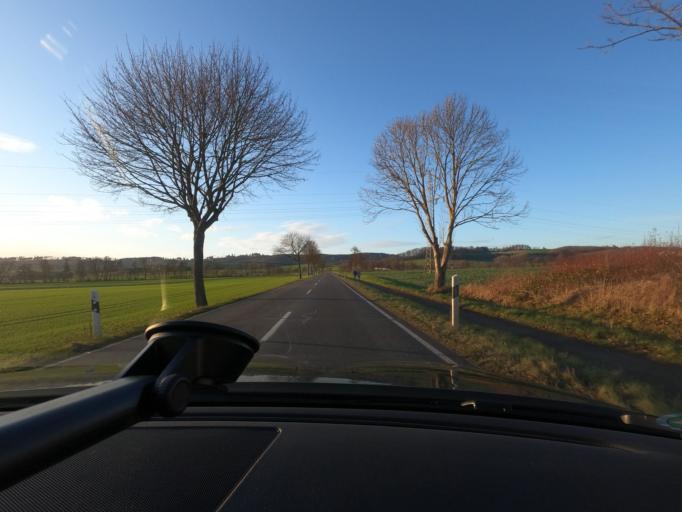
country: DE
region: Lower Saxony
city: Badenhausen
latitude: 51.7689
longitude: 10.1899
